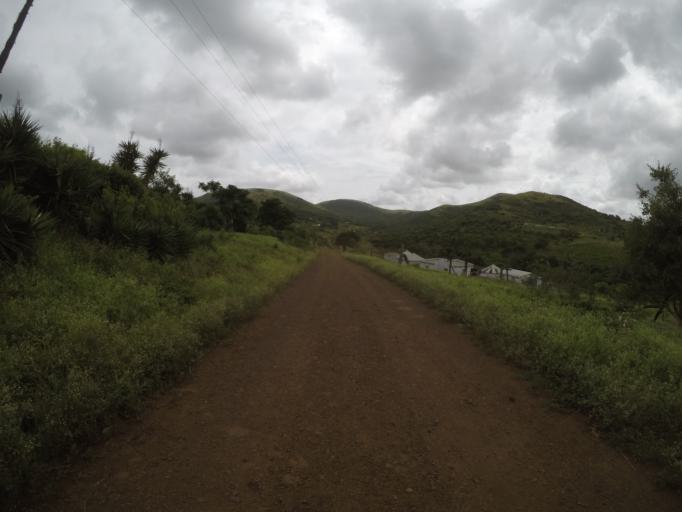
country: ZA
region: KwaZulu-Natal
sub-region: uThungulu District Municipality
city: Empangeni
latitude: -28.5878
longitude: 31.8887
